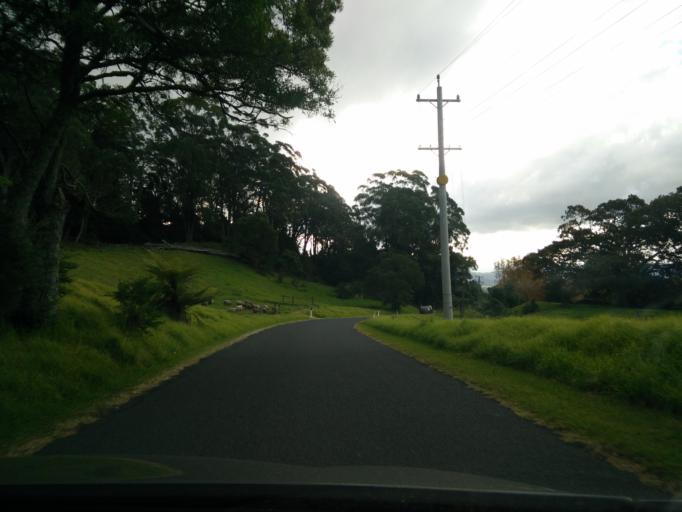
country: AU
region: New South Wales
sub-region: Kiama
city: Jamberoo
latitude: -34.6925
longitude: 150.7885
